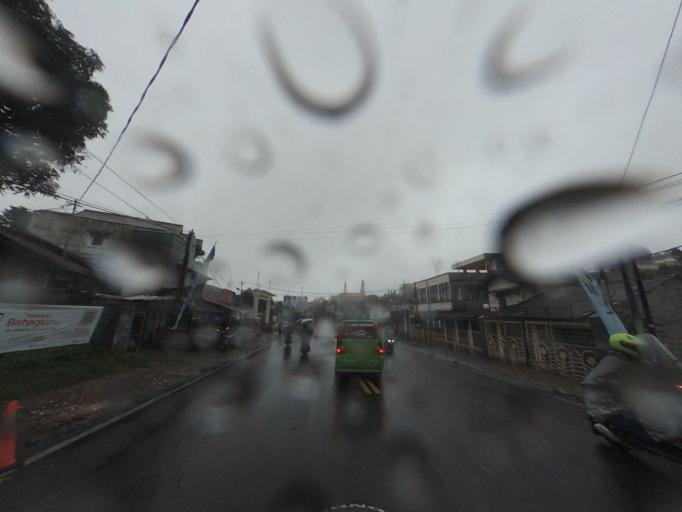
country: ID
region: West Java
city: Caringin
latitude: -6.6563
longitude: 106.8588
